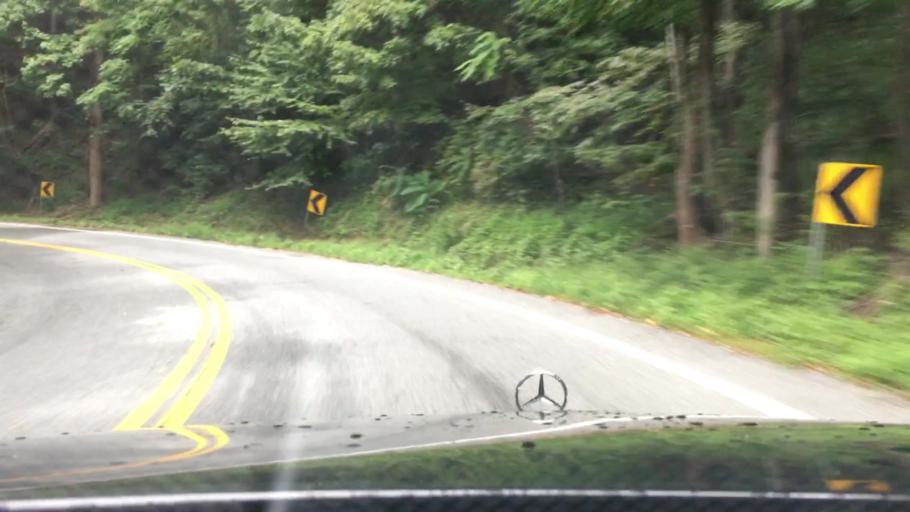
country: US
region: Virginia
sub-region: Nelson County
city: Nellysford
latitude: 37.8513
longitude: -78.9274
